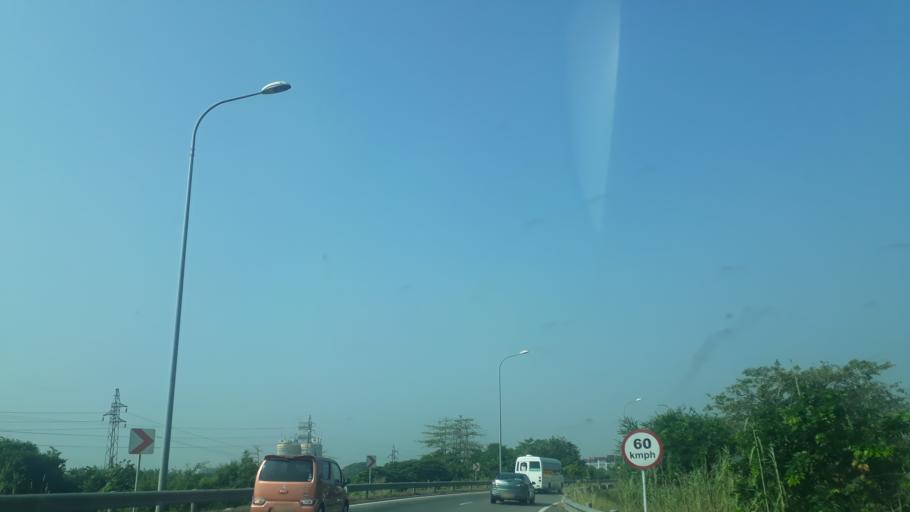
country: LK
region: Western
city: Peliyagoda
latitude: 6.9675
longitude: 79.8944
